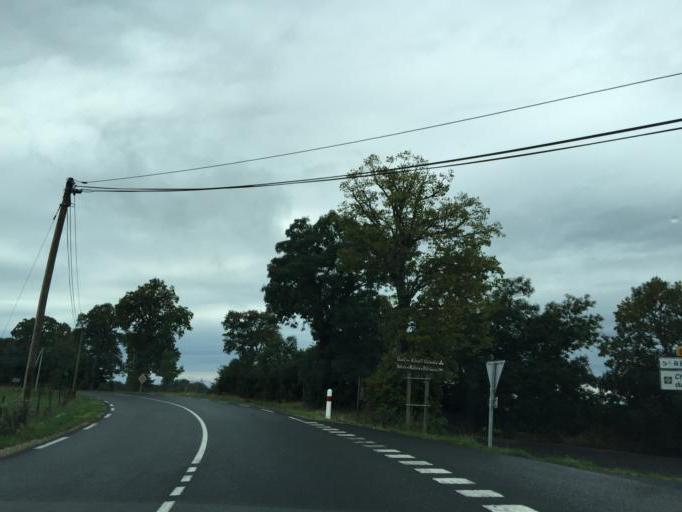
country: FR
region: Midi-Pyrenees
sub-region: Departement de l'Aveyron
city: Laguiole
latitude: 44.6228
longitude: 2.8175
